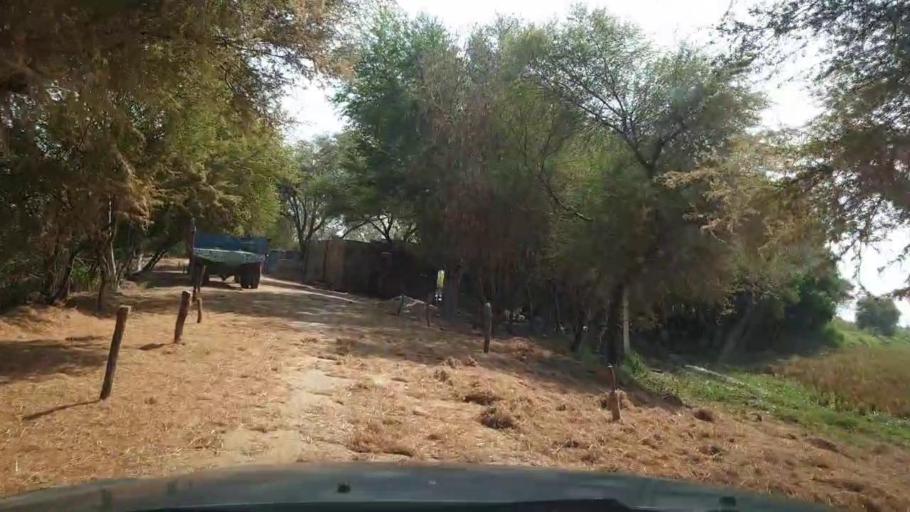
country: PK
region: Sindh
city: Bulri
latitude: 24.8807
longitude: 68.4038
